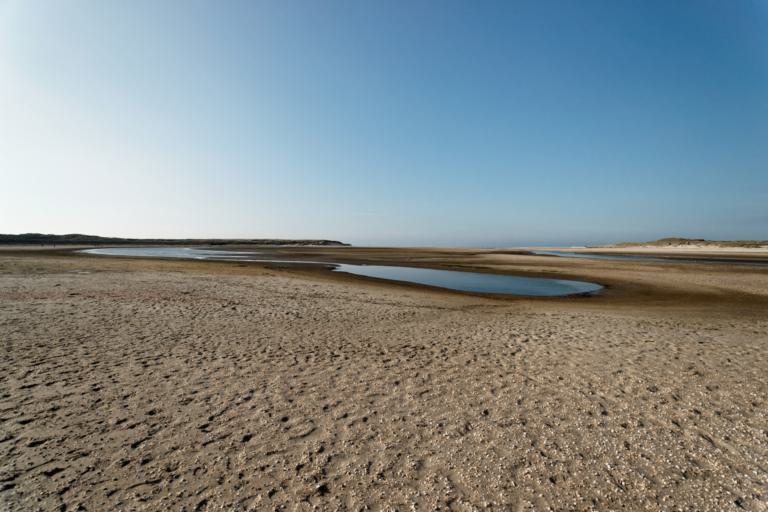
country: NL
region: North Holland
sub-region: Gemeente Texel
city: Den Burg
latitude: 53.1343
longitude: 4.8051
